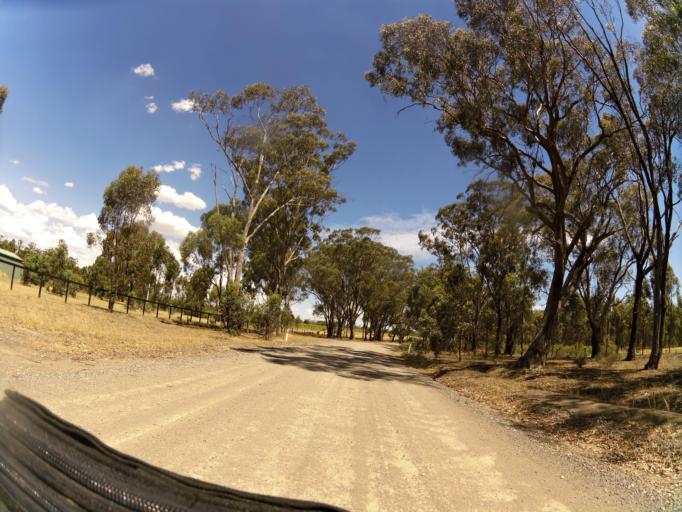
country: AU
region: Victoria
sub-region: Campaspe
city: Kyabram
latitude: -36.8168
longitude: 145.0802
